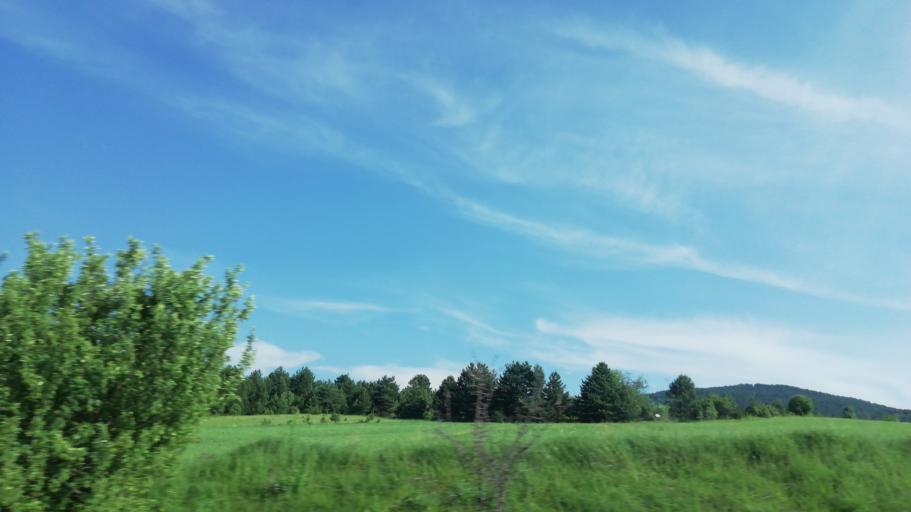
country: TR
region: Karabuk
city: Karabuk
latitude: 41.0923
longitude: 32.5899
